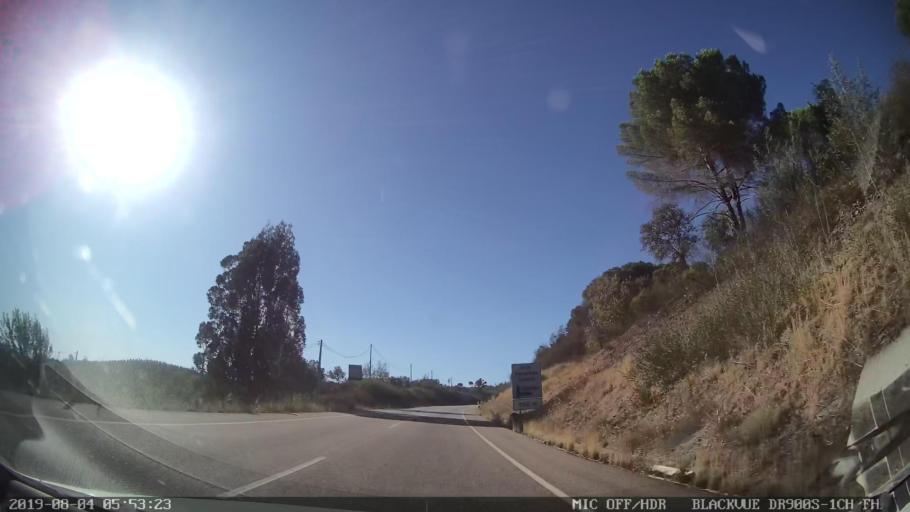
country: PT
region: Portalegre
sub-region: Gaviao
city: Gaviao
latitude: 39.4535
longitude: -7.9285
